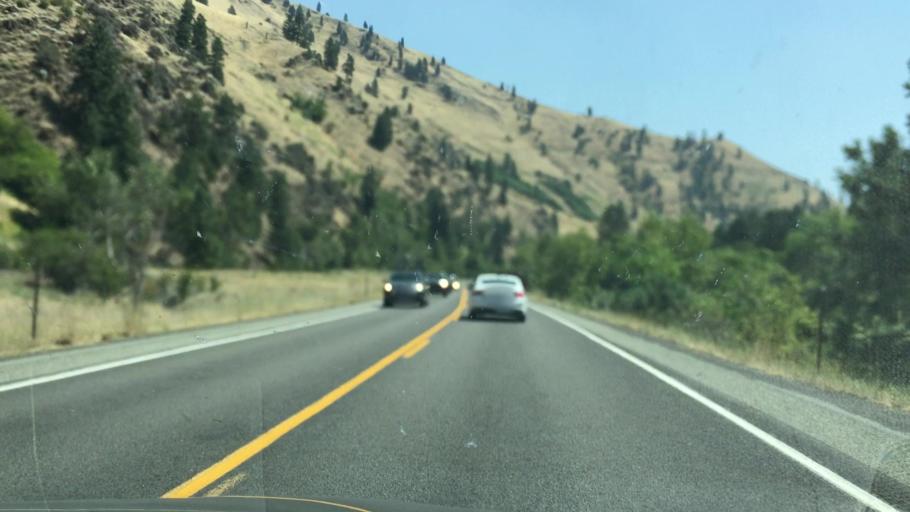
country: US
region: Idaho
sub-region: Valley County
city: McCall
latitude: 45.2854
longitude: -116.3519
